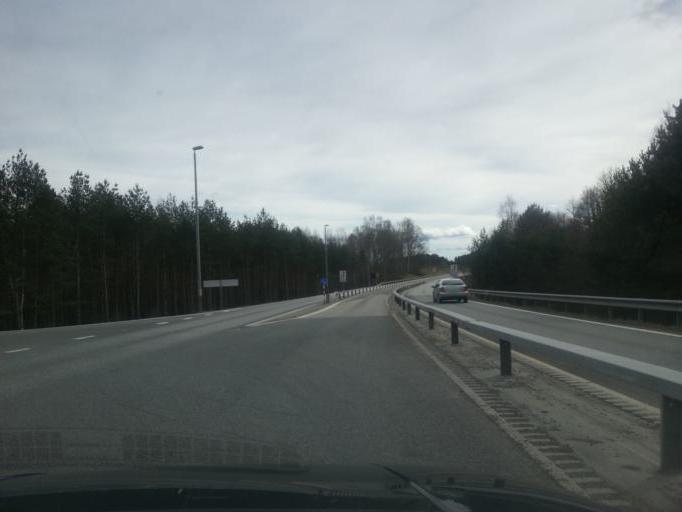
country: SE
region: Joenkoeping
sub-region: Jonkopings Kommun
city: Bankeryd
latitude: 57.8654
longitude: 14.1041
